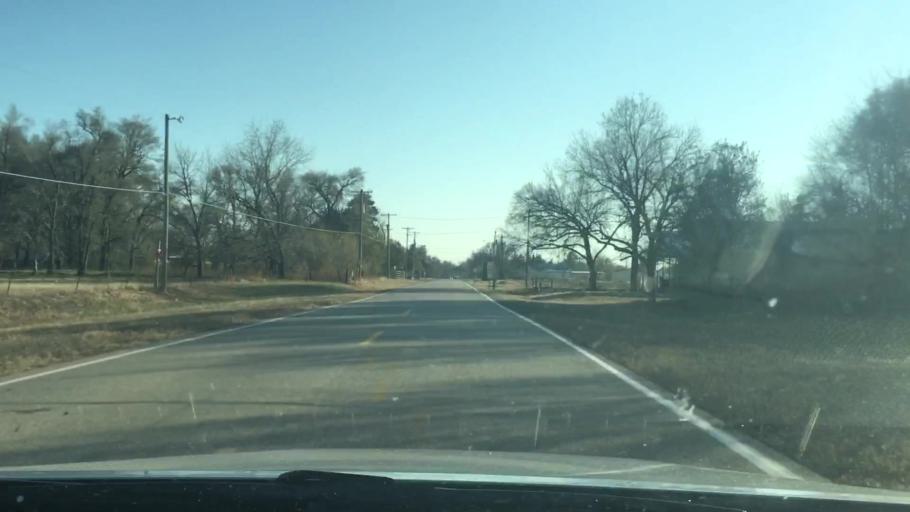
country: US
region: Kansas
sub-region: Reno County
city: Nickerson
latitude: 38.1568
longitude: -98.0874
